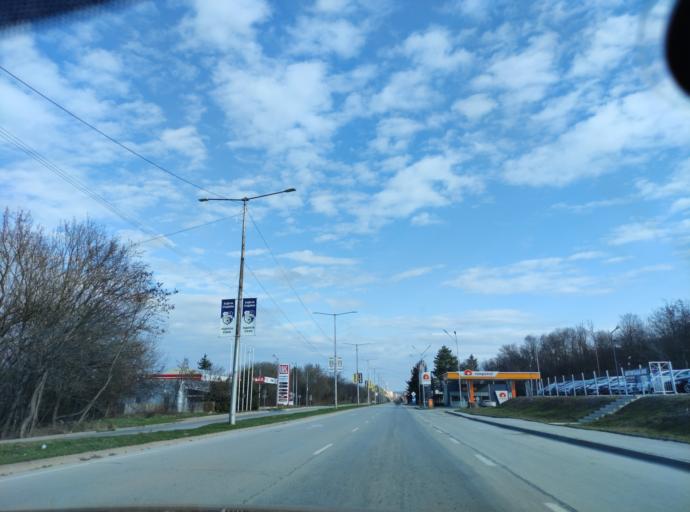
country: BG
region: Pleven
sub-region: Obshtina Pleven
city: Pleven
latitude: 43.4325
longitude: 24.5804
